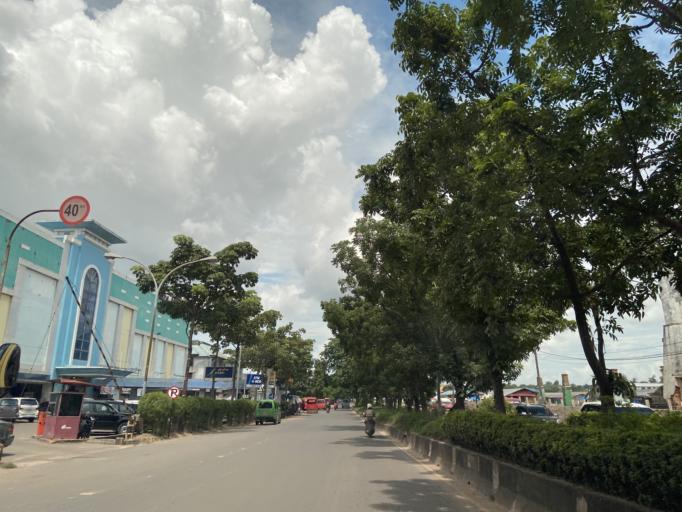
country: SG
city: Singapore
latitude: 1.1476
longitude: 104.0034
